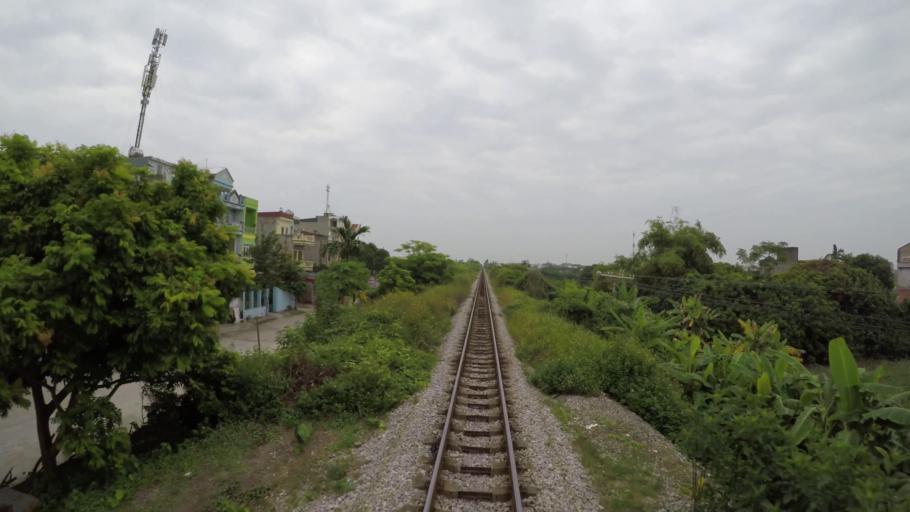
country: VN
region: Hai Duong
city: Thanh Pho Hai Duong
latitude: 20.9436
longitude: 106.3594
